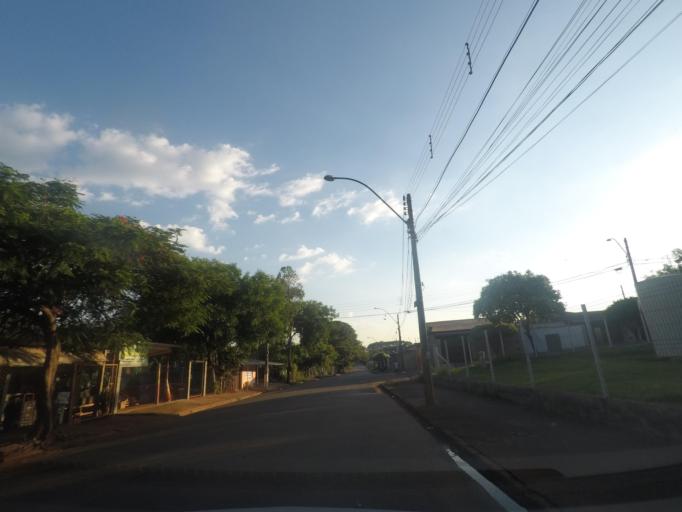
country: BR
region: Sao Paulo
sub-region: Sumare
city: Sumare
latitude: -22.8164
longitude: -47.2797
